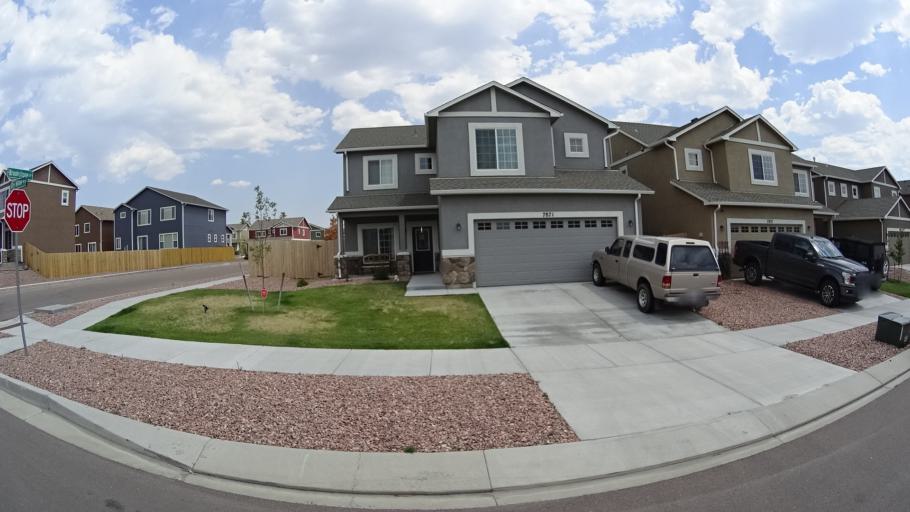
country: US
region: Colorado
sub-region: El Paso County
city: Black Forest
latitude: 38.9464
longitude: -104.6868
